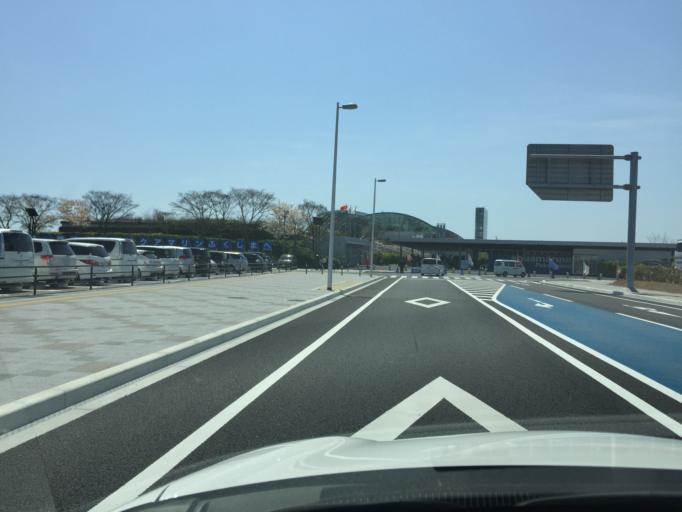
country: JP
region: Fukushima
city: Iwaki
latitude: 36.9454
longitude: 140.9015
